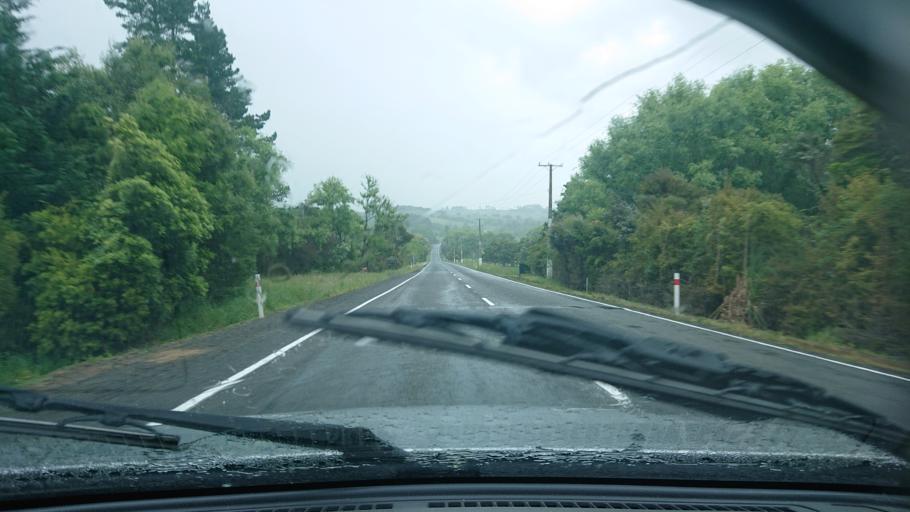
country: NZ
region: Auckland
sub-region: Auckland
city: Wellsford
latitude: -36.3144
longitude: 174.4944
